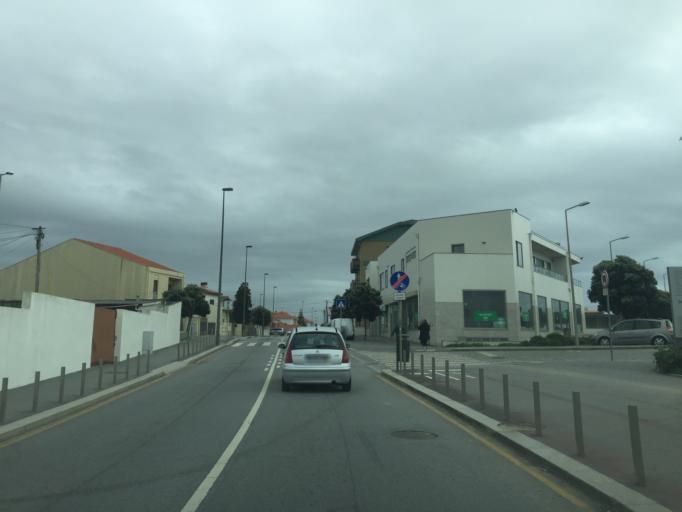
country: PT
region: Porto
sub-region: Matosinhos
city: Lavra
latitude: 41.2384
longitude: -8.7230
